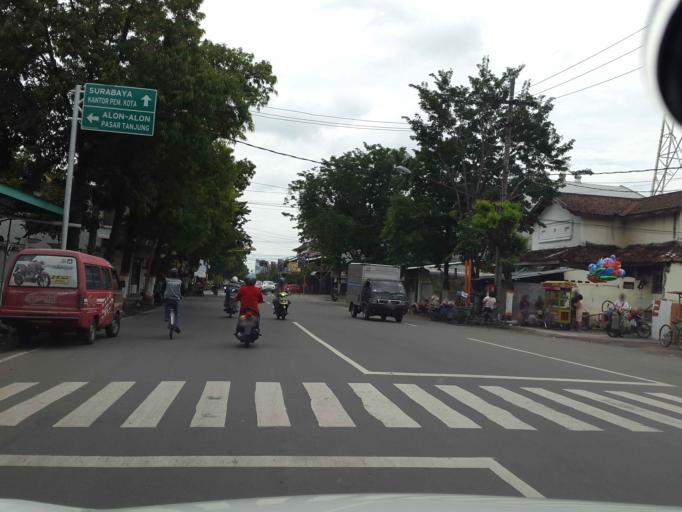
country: ID
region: East Java
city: Mojokerto
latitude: -7.4718
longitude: 112.4334
